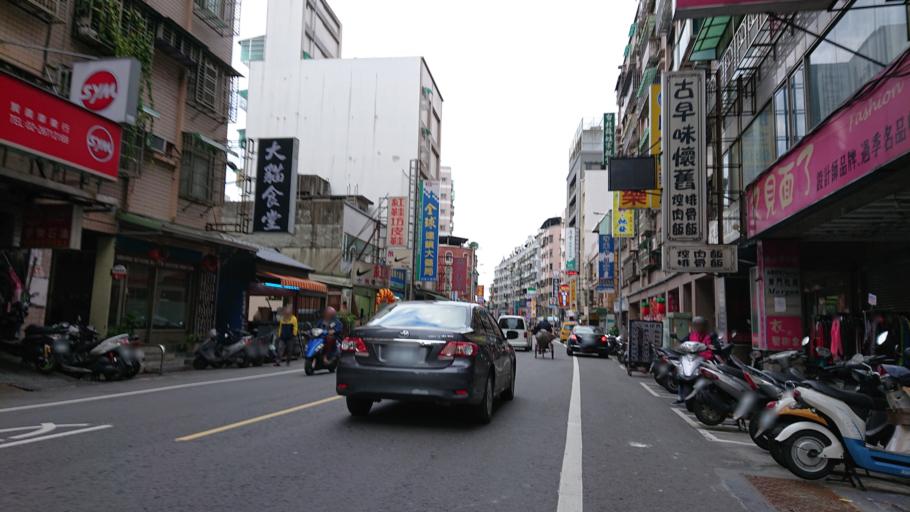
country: TW
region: Taiwan
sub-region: Taoyuan
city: Taoyuan
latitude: 24.9283
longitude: 121.3767
